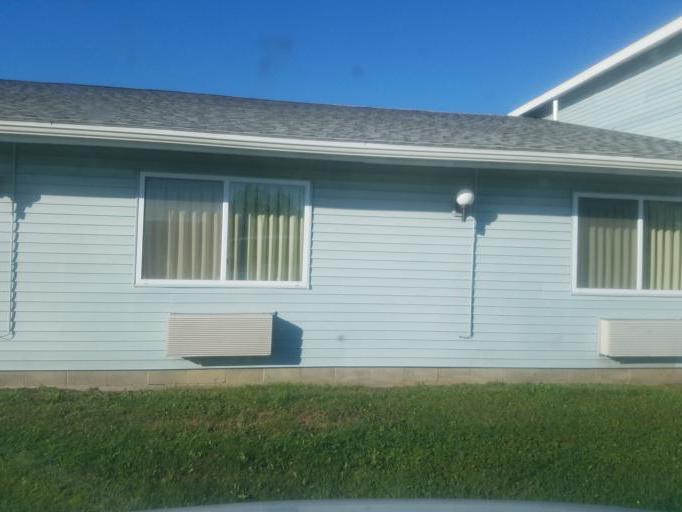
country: US
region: New York
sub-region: Allegany County
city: Cuba
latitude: 42.2267
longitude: -78.2725
